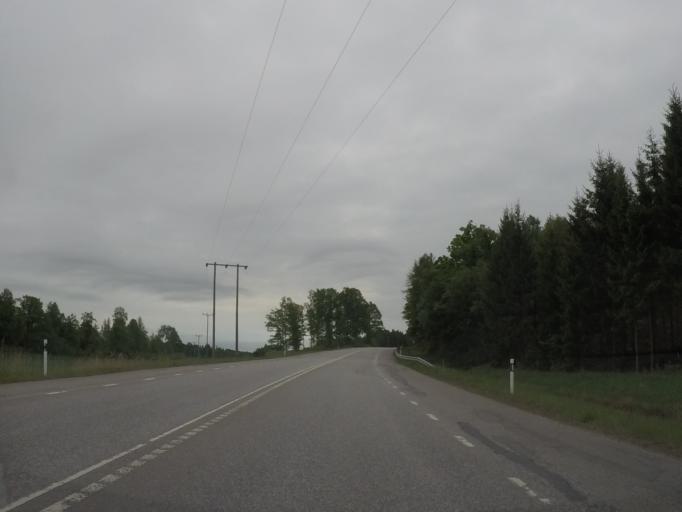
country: SE
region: Soedermanland
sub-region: Nykopings Kommun
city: Stigtomta
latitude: 58.8316
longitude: 16.7520
